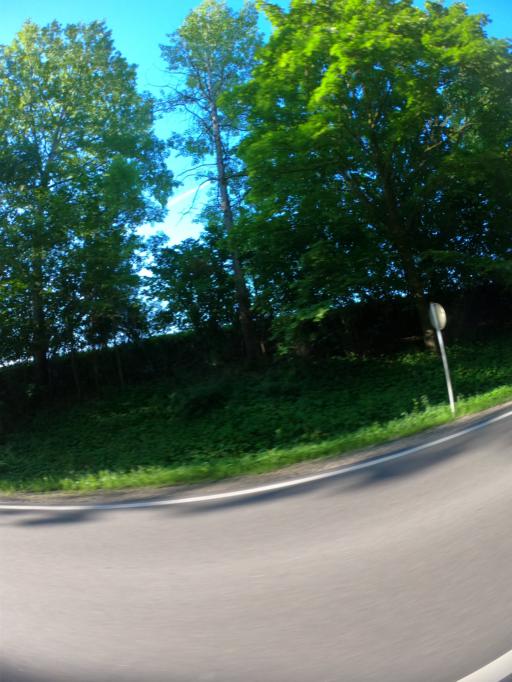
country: DE
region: Bavaria
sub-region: Upper Bavaria
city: Inning am Holz
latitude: 48.3357
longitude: 12.0520
